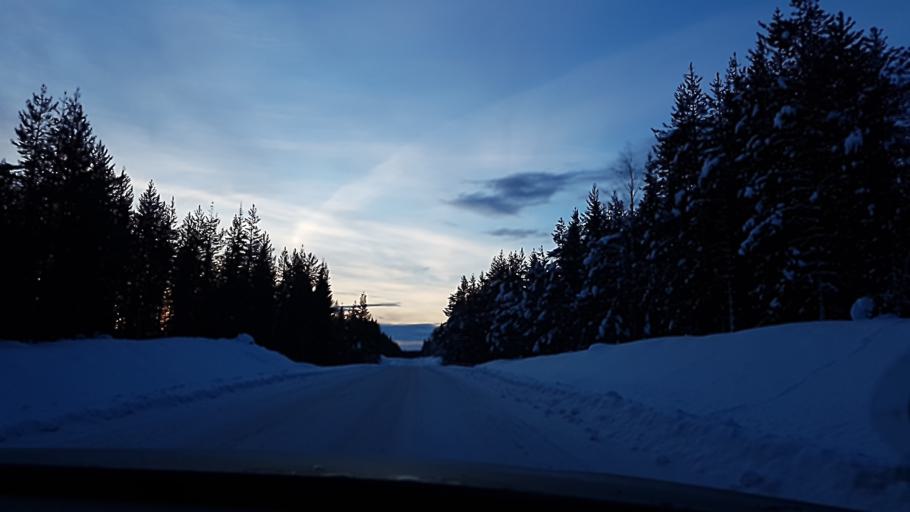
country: SE
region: Norrbotten
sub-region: Arvidsjaurs Kommun
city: Arvidsjaur
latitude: 65.9353
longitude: 19.4629
